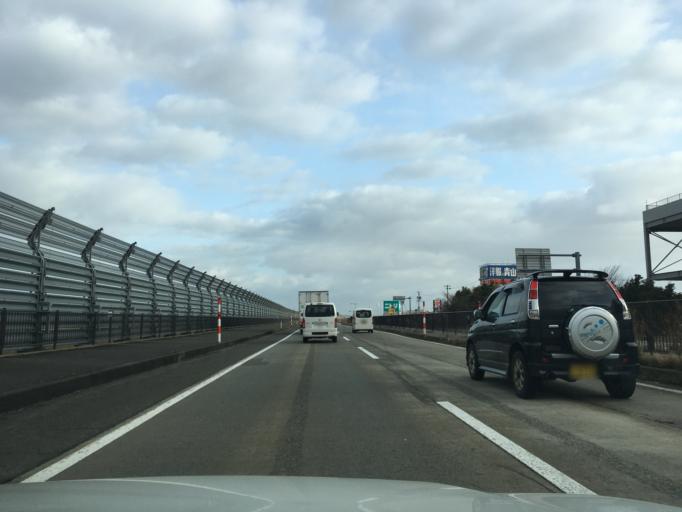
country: JP
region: Yamagata
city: Tsuruoka
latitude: 38.8155
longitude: 139.8328
